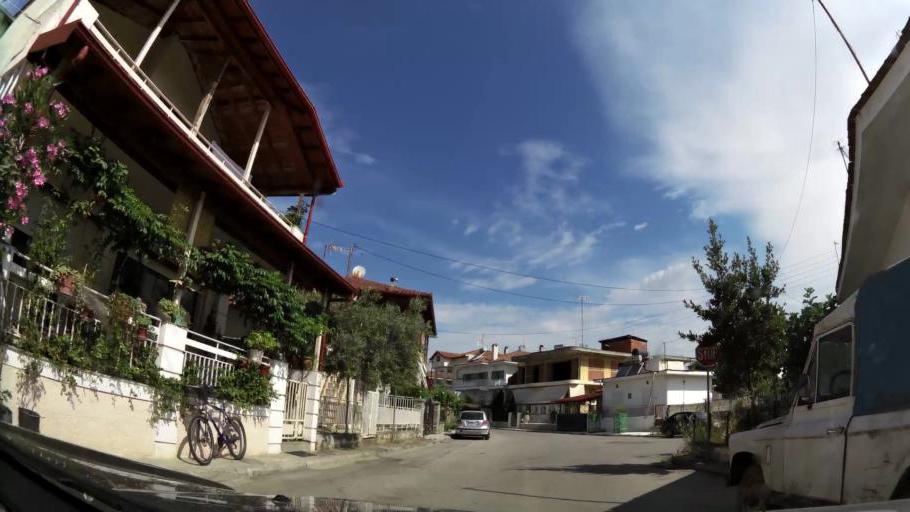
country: GR
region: Central Macedonia
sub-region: Nomos Pierias
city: Katerini
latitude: 40.2731
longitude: 22.4905
